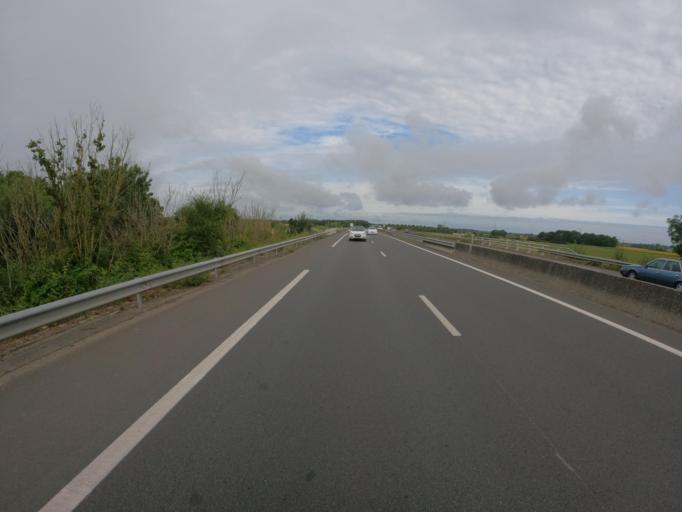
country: FR
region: Centre
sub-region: Departement d'Indre-et-Loire
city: Villandry
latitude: 47.3040
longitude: 0.5240
